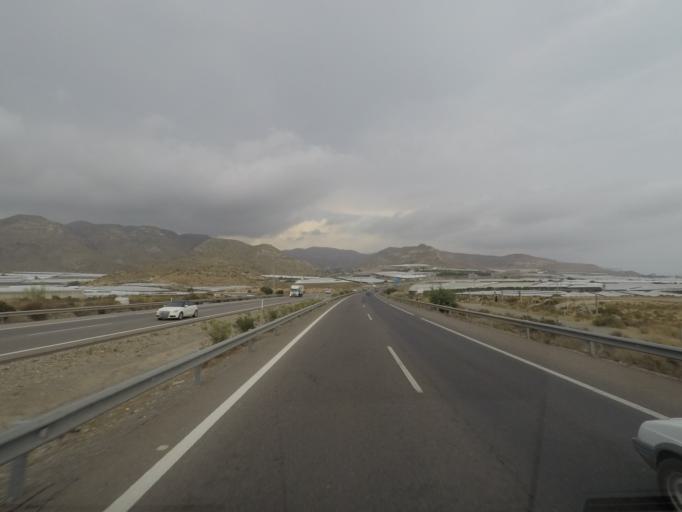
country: ES
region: Andalusia
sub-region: Provincia de Almeria
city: Vicar
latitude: 36.8092
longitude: -2.6673
